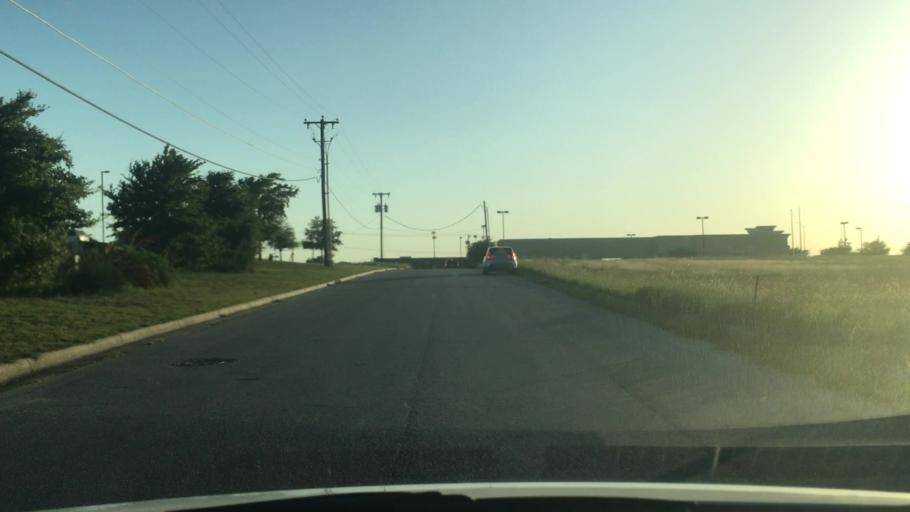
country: US
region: Texas
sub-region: Travis County
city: Windemere
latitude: 30.4849
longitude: -97.6474
